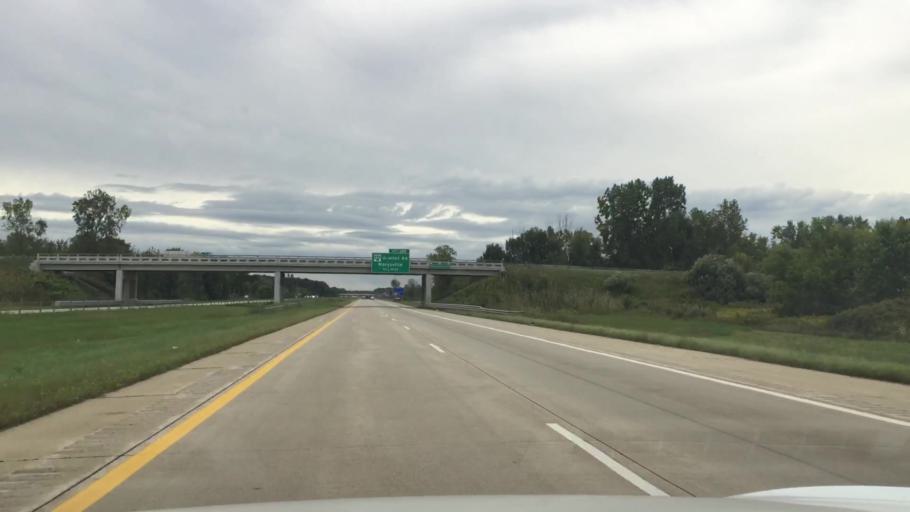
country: US
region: Michigan
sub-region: Saint Clair County
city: Marysville
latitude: 42.9363
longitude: -82.5071
